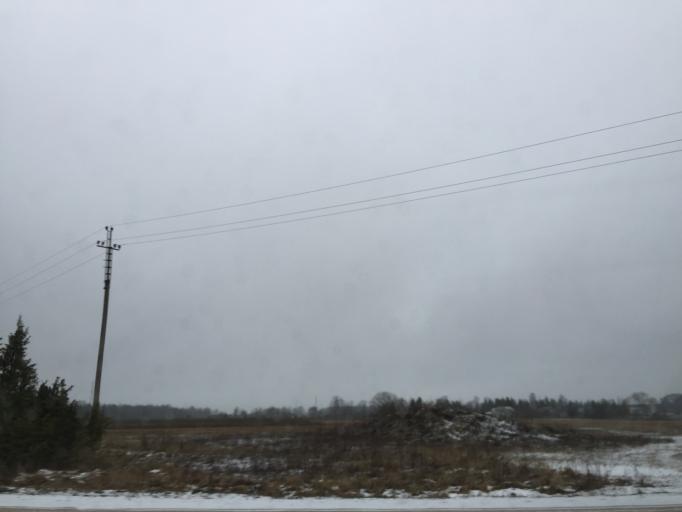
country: EE
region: Laeaene
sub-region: Lihula vald
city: Lihula
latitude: 58.5747
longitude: 23.5425
